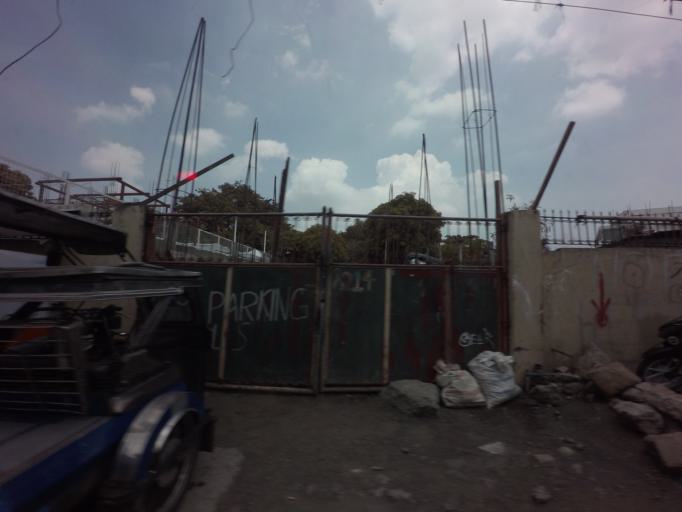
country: PH
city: Sambayanihan People's Village
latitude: 14.4307
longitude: 121.0500
